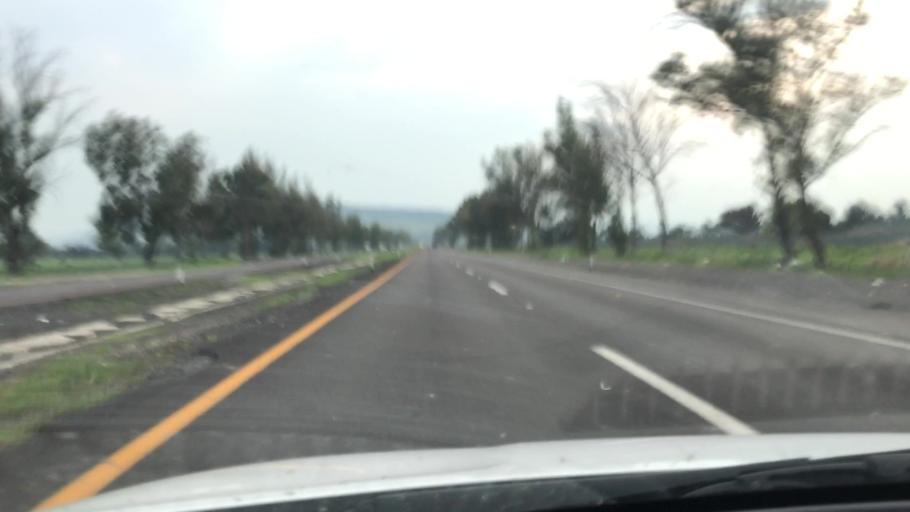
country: MX
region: Jalisco
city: Ocotlan
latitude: 20.3877
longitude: -102.7120
